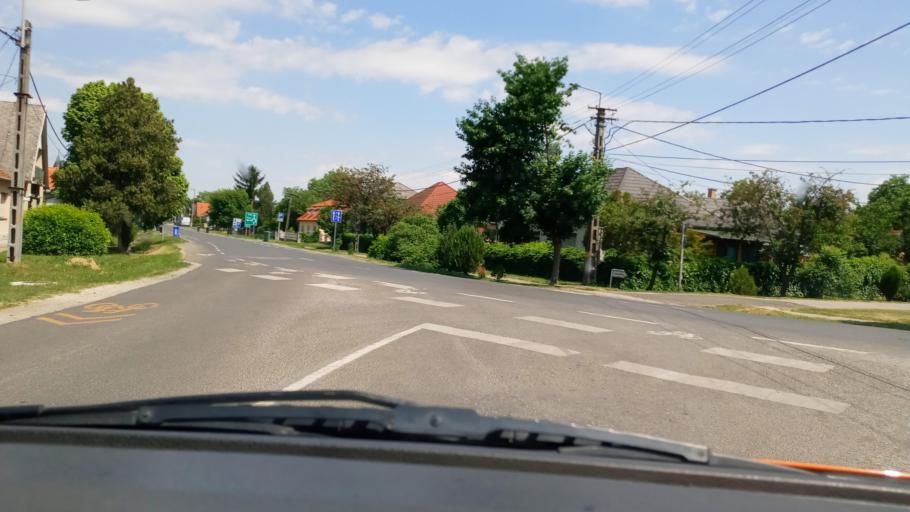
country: HU
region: Baranya
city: Harkany
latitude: 45.8463
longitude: 18.2342
